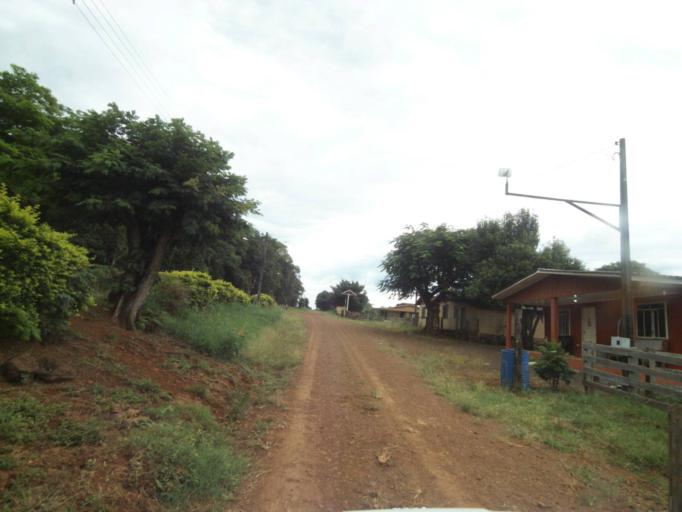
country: BR
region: Parana
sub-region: Guaraniacu
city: Guaraniacu
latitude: -24.9146
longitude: -52.9375
